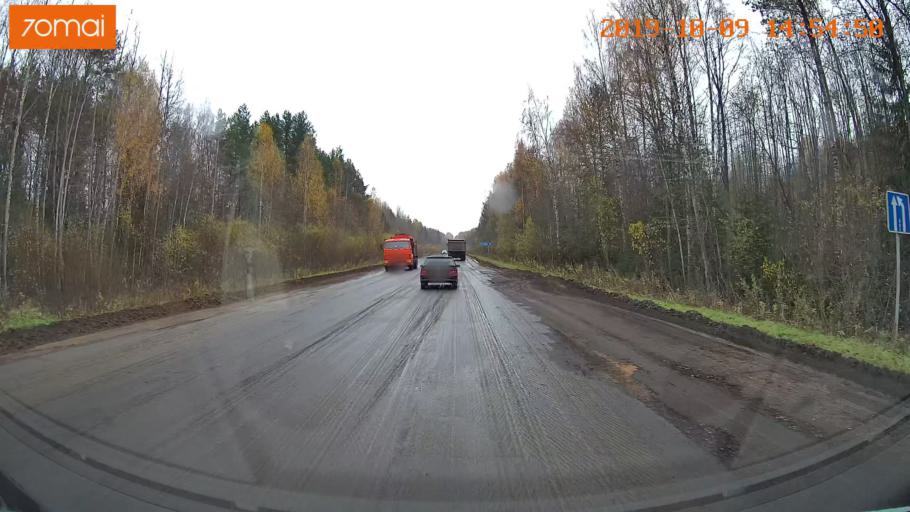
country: RU
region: Kostroma
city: Chistyye Bory
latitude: 58.3541
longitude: 41.6439
